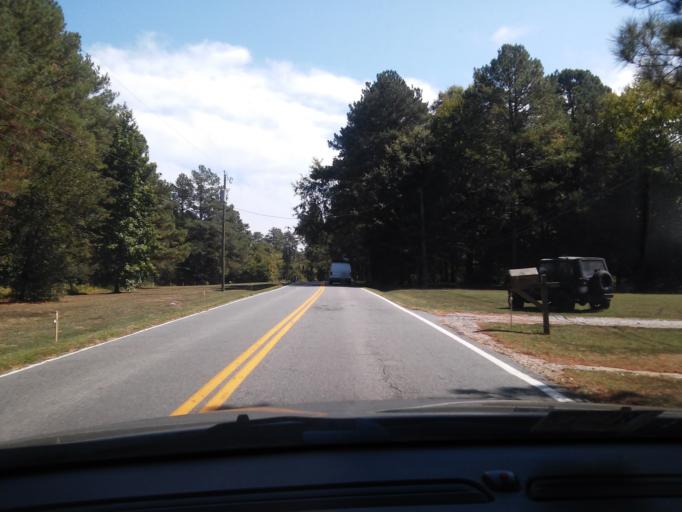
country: US
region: Virginia
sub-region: Henrico County
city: Short Pump
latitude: 37.5581
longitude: -77.6799
